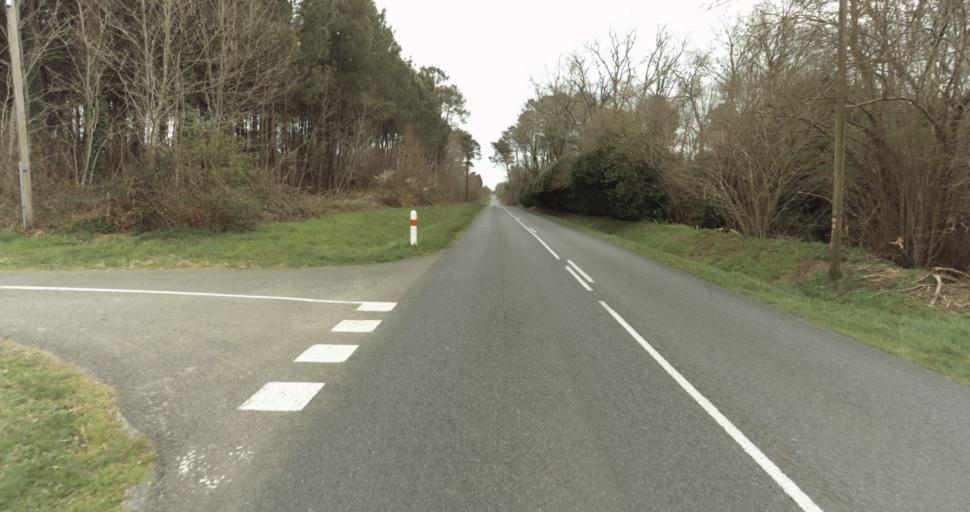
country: FR
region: Aquitaine
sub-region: Departement des Landes
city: Roquefort
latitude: 44.0661
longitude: -0.4170
